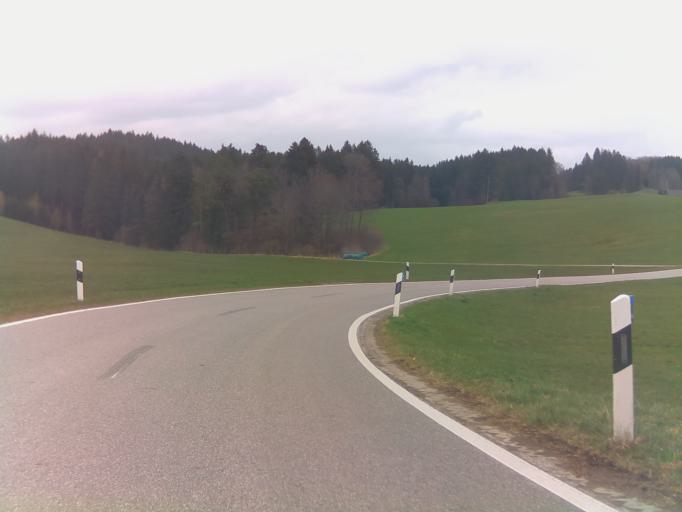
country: DE
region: Bavaria
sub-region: Upper Bavaria
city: Bad Kohlgrub
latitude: 47.7133
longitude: 11.0793
